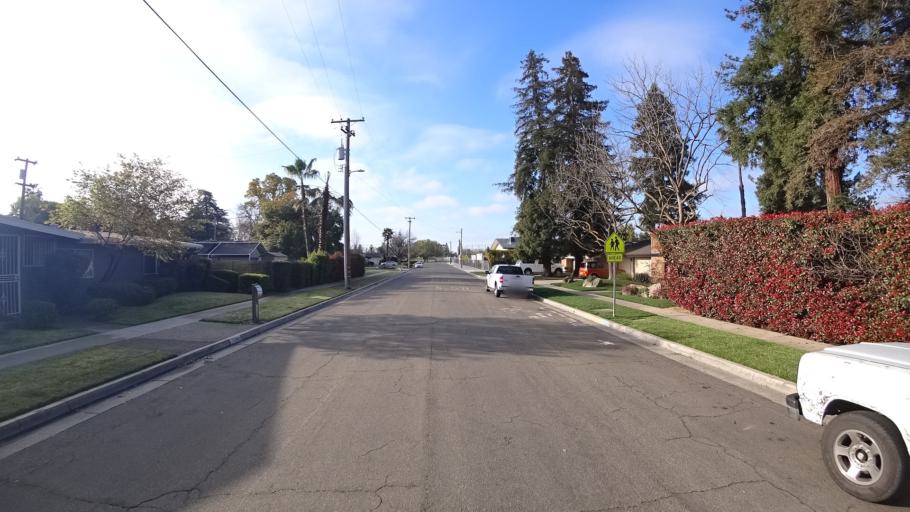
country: US
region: California
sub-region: Fresno County
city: Fresno
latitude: 36.8191
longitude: -119.7971
